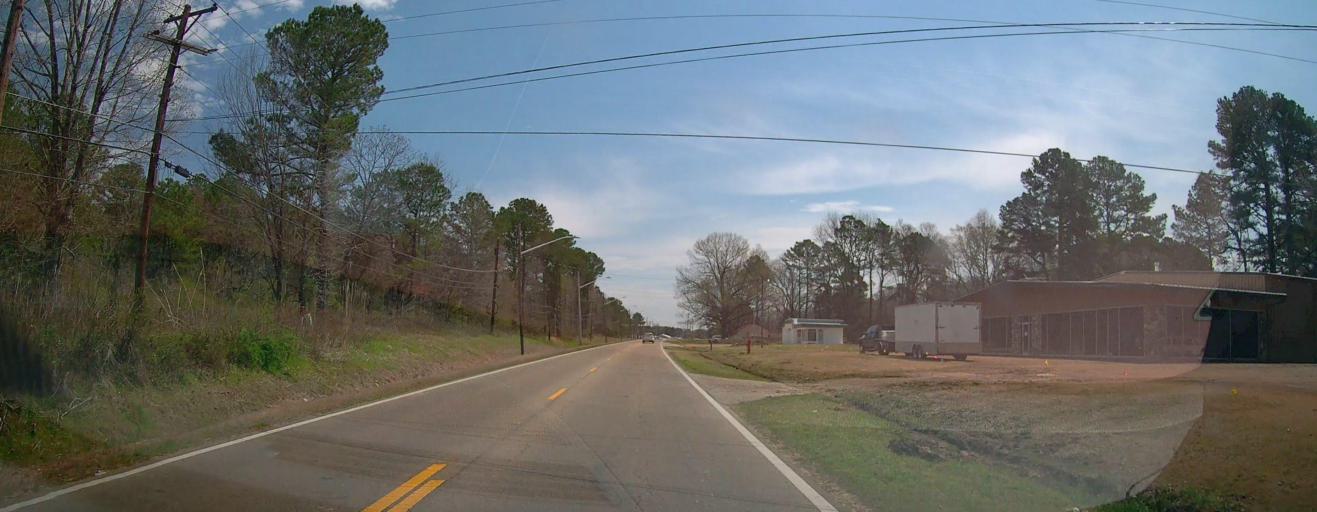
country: US
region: Mississippi
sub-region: Union County
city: New Albany
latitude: 34.5142
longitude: -89.0422
